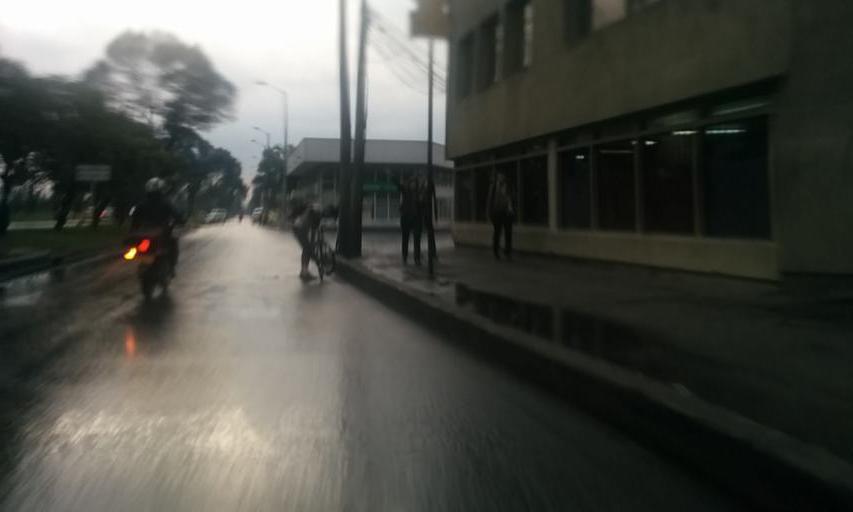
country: CO
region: Bogota D.C.
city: Bogota
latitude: 4.6270
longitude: -74.0997
